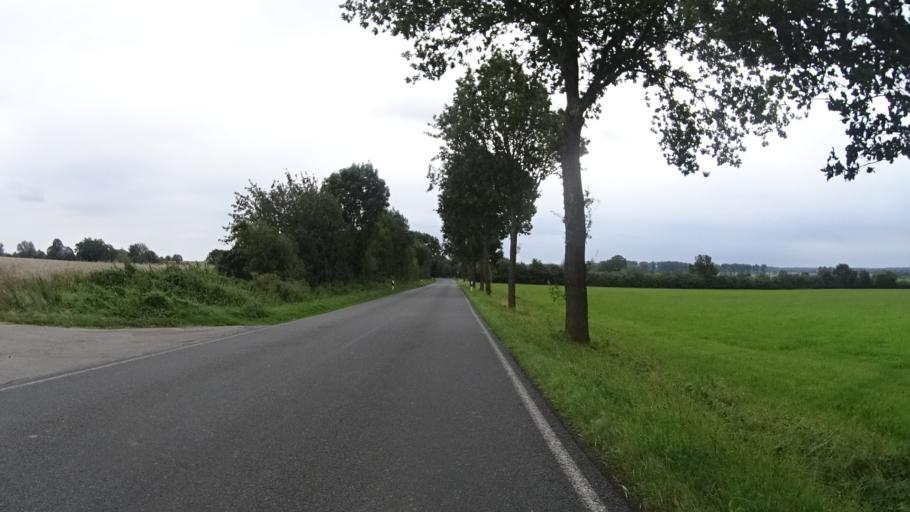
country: DE
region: Schleswig-Holstein
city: Duvensee
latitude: 53.7108
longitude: 10.5616
